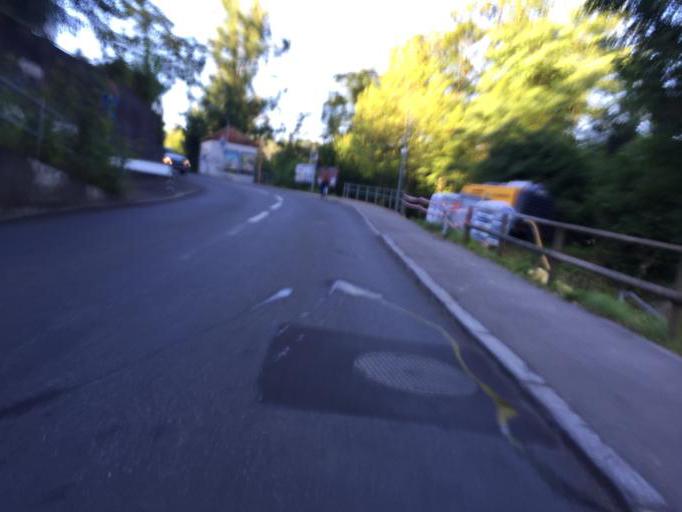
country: CH
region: Bern
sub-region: Bern-Mittelland District
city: Bern
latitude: 46.9734
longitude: 7.4413
